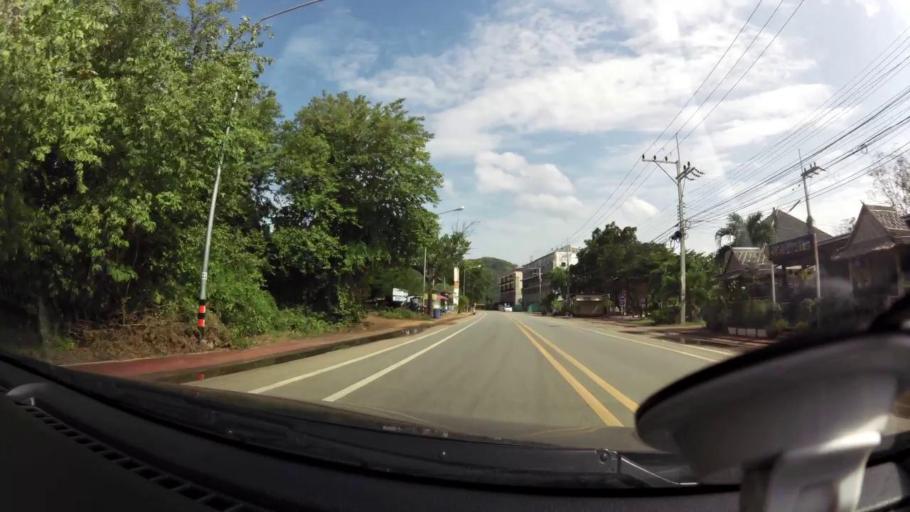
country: TH
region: Prachuap Khiri Khan
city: Pran Buri
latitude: 12.4631
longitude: 99.9744
